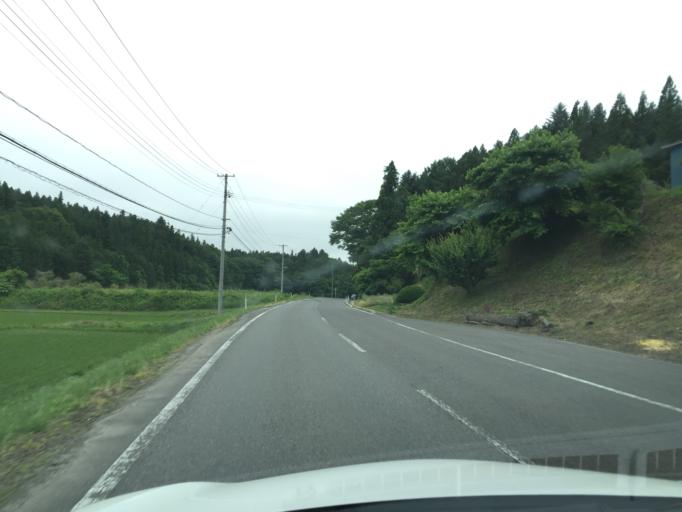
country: JP
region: Fukushima
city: Funehikimachi-funehiki
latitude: 37.3131
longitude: 140.6202
